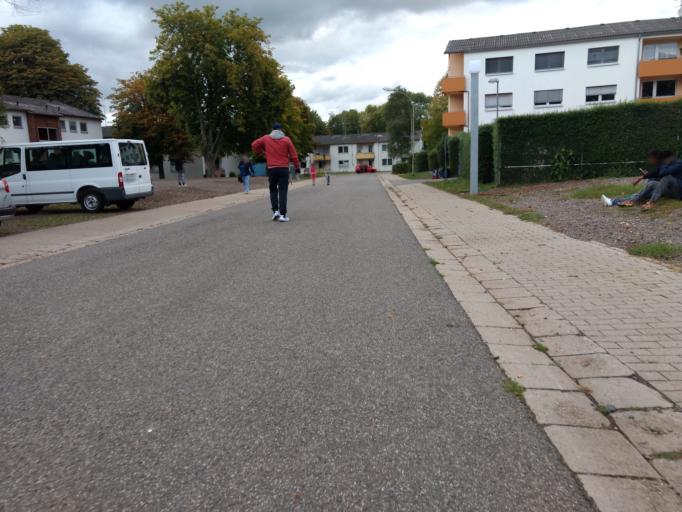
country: DE
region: Saarland
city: Lebach
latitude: 49.4049
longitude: 6.8993
